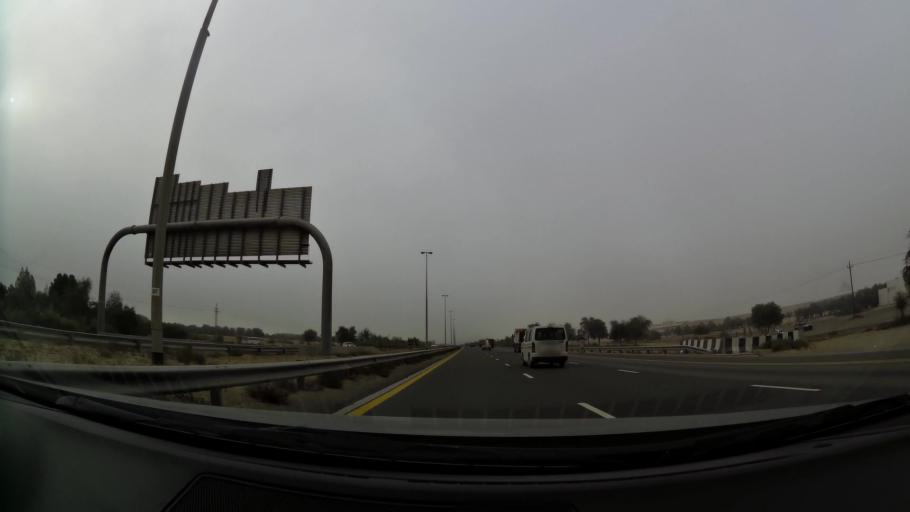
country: AE
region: Dubai
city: Dubai
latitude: 25.0759
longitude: 55.4015
